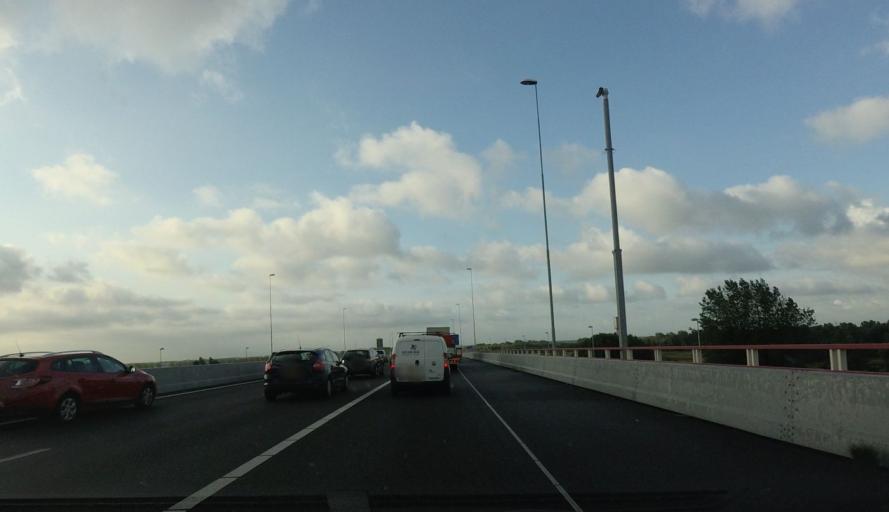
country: NL
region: North Holland
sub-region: Gemeente Haarlem
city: Haarlem
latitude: 52.3836
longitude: 4.7077
